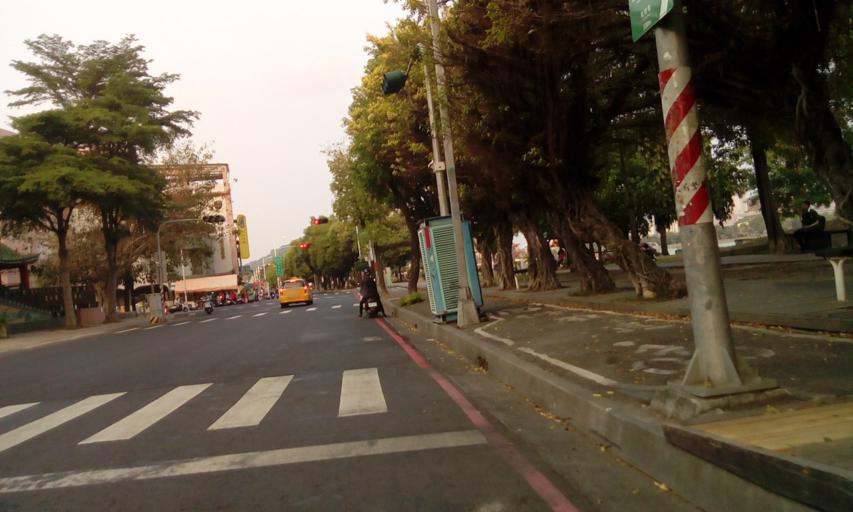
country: TW
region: Kaohsiung
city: Kaohsiung
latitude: 22.6828
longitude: 120.2929
